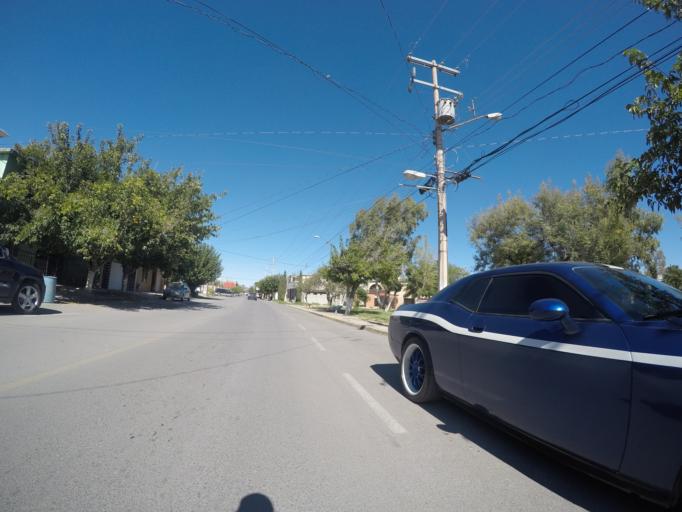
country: MX
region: Chihuahua
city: Ciudad Juarez
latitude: 31.7180
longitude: -106.4191
